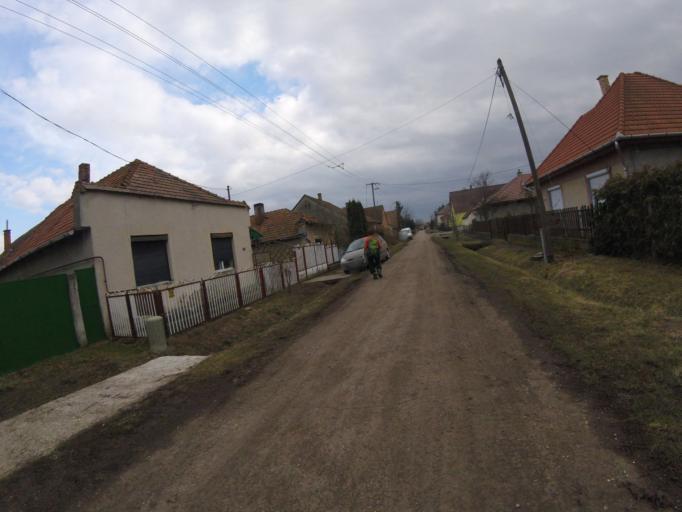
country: HU
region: Heves
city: Egerszalok
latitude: 47.8343
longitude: 20.3281
